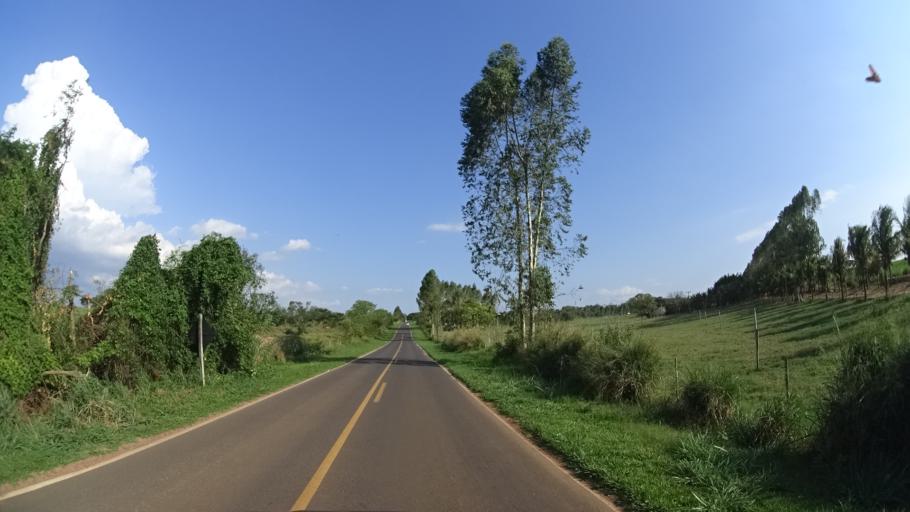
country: BR
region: Sao Paulo
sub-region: Urupes
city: Urupes
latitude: -21.3654
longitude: -49.4754
